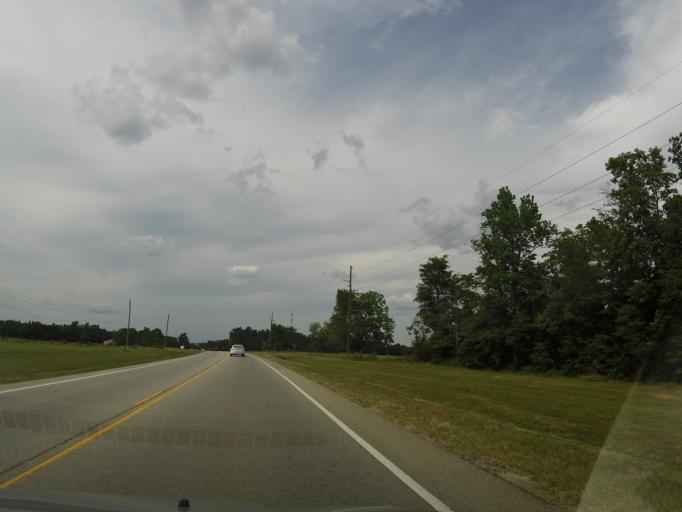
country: US
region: Georgia
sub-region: Jefferson County
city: Louisville
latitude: 33.0795
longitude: -82.4043
